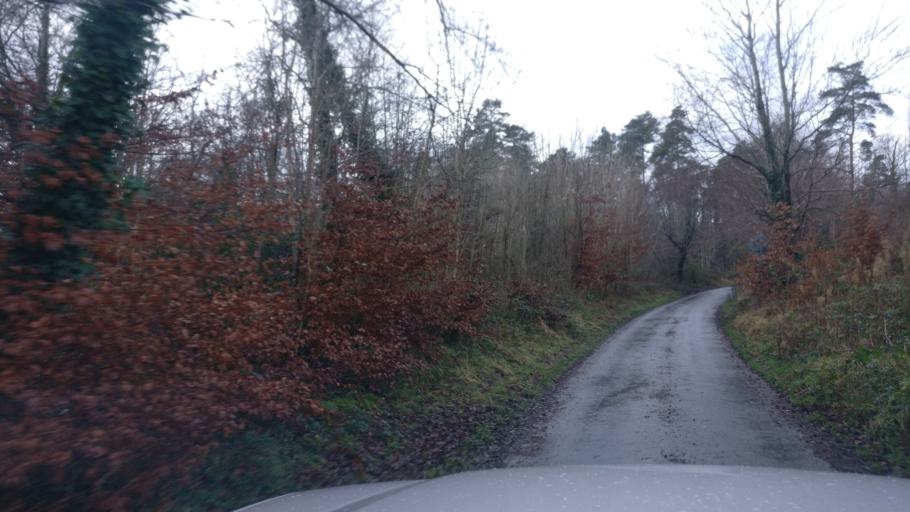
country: IE
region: Connaught
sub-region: County Galway
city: Loughrea
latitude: 53.2429
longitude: -8.6527
